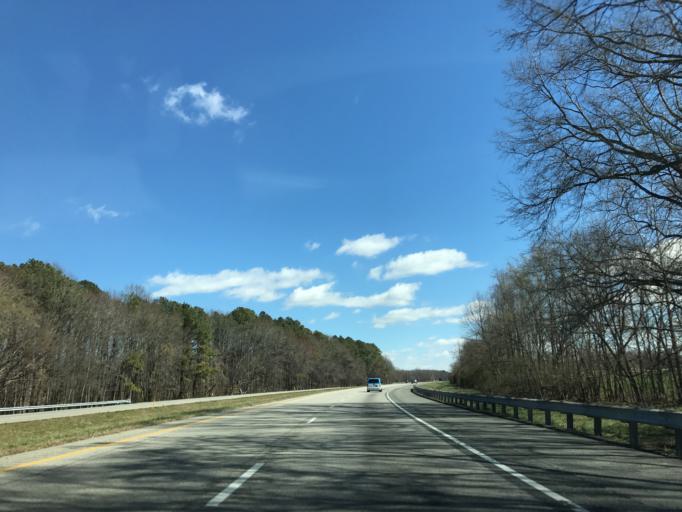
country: US
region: Maryland
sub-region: Queen Anne's County
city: Centreville
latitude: 39.0125
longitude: -76.1040
